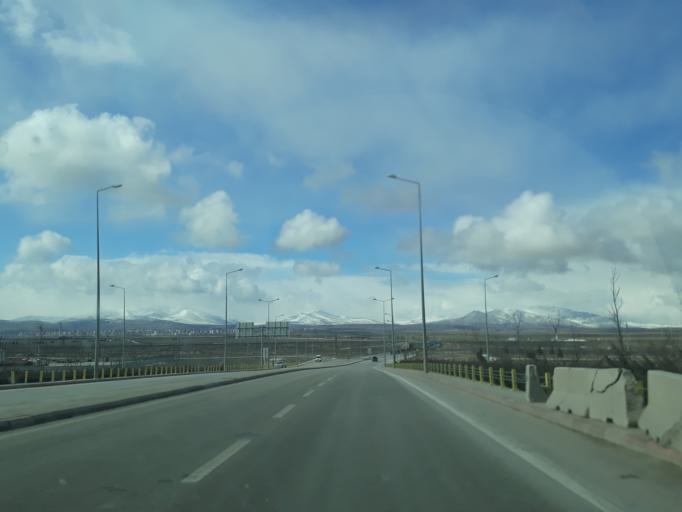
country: TR
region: Konya
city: Asagipinarbasi
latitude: 37.9909
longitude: 32.5941
